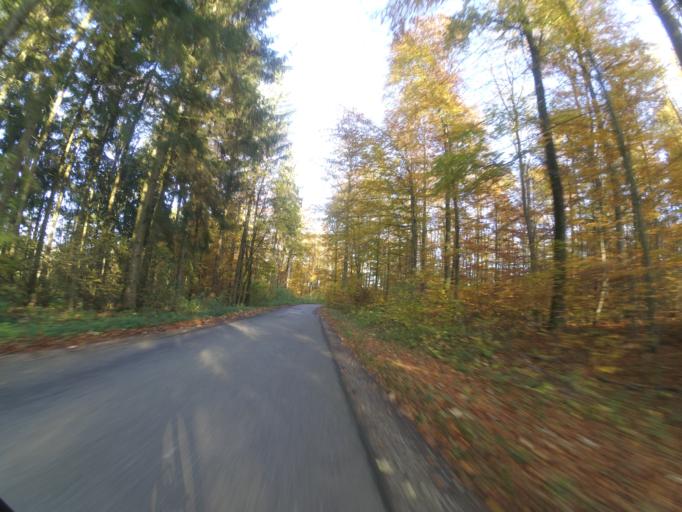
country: DE
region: Baden-Wuerttemberg
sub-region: Tuebingen Region
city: Berghulen
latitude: 48.4783
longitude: 9.8017
